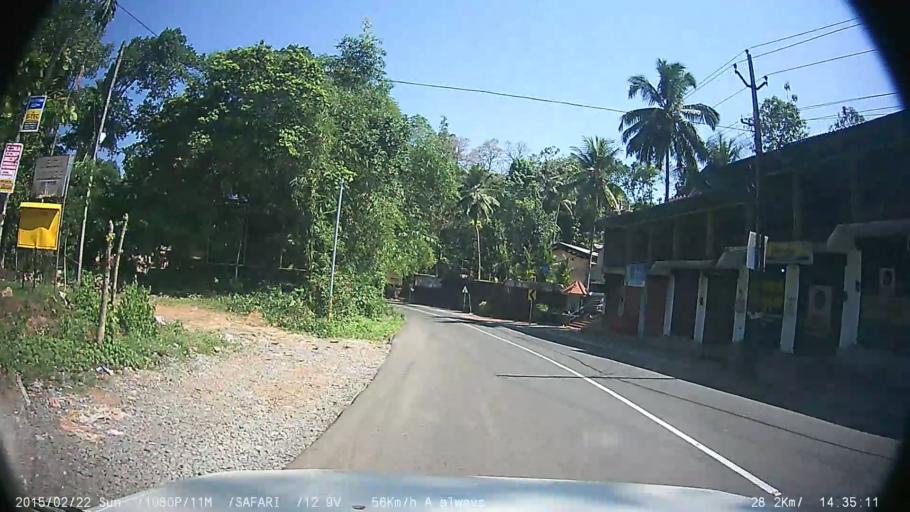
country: IN
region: Kerala
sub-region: Kottayam
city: Erattupetta
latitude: 9.5593
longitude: 76.7796
